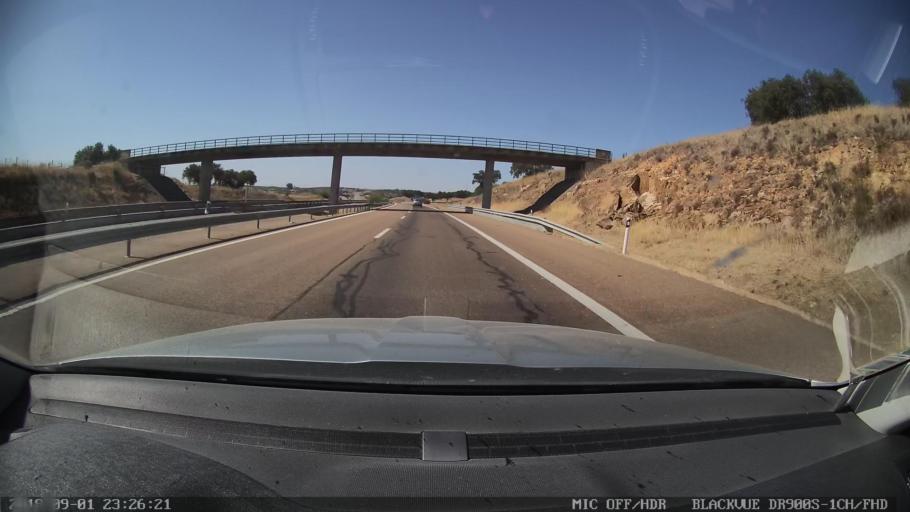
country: PT
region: Portalegre
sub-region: Elvas
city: Elvas
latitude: 38.8972
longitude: -7.2022
